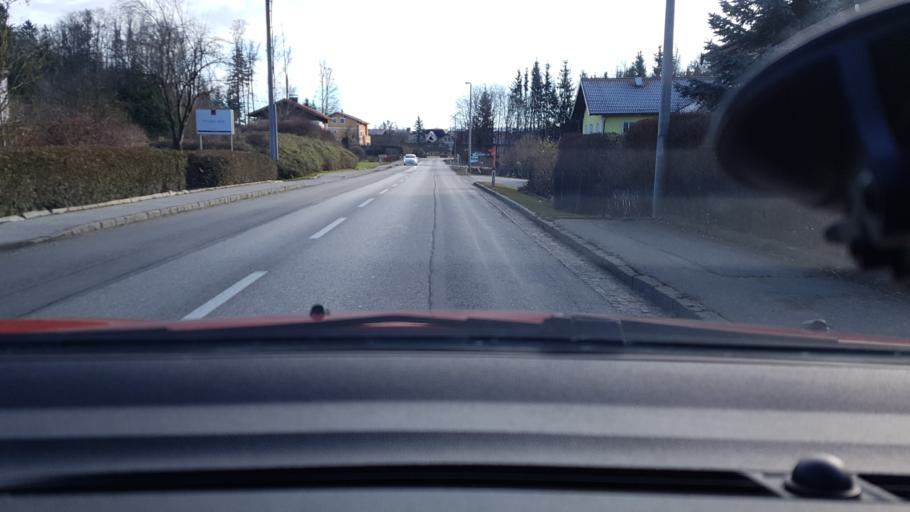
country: AT
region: Salzburg
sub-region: Politischer Bezirk Salzburg-Umgebung
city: Dorfbeuern
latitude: 48.0500
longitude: 12.9864
